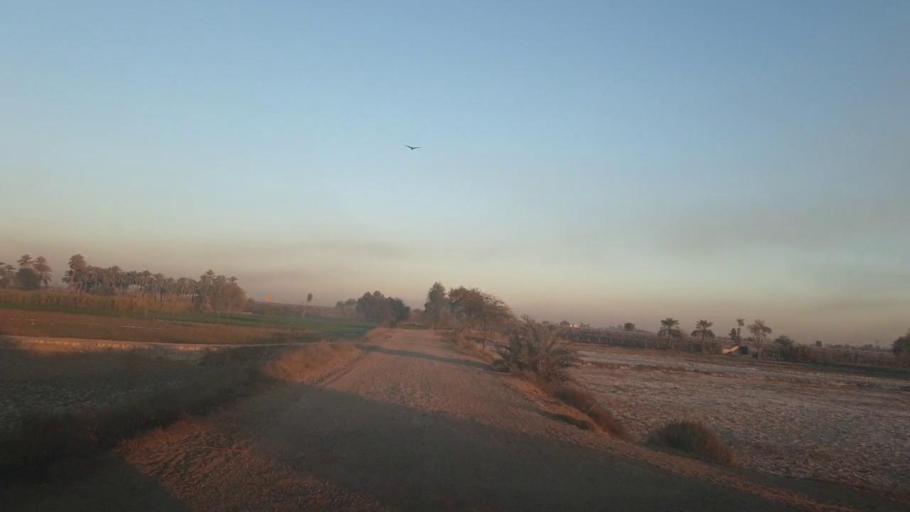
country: PK
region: Sindh
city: Ghotki
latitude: 28.0335
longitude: 69.3069
